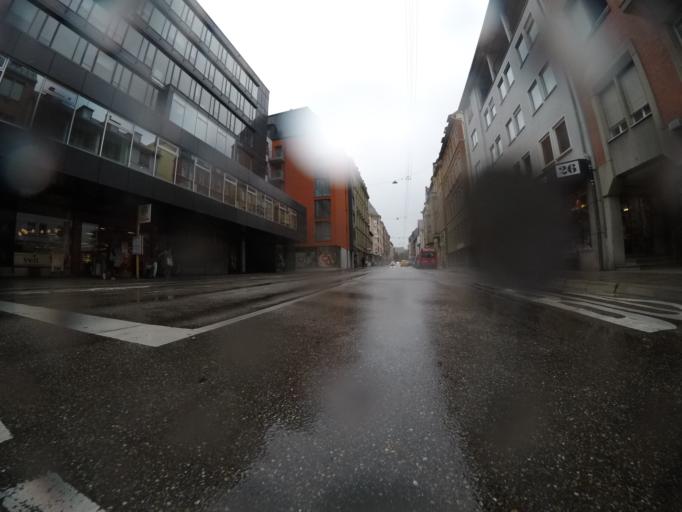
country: DE
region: Baden-Wuerttemberg
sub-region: Regierungsbezirk Stuttgart
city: Stuttgart
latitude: 48.7707
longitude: 9.1580
